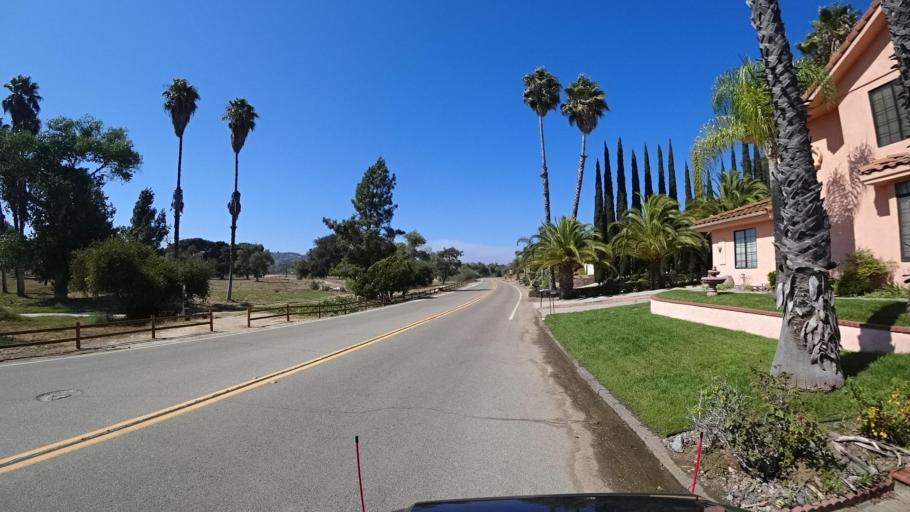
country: US
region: California
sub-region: San Diego County
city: Bonsall
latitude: 33.2904
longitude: -117.2164
